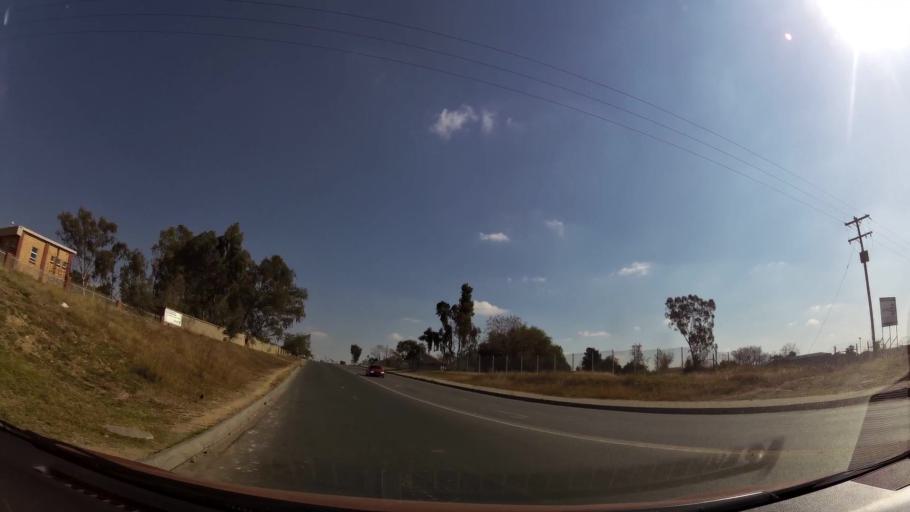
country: ZA
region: Gauteng
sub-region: West Rand District Municipality
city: Muldersdriseloop
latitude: -26.0222
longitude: 27.9420
